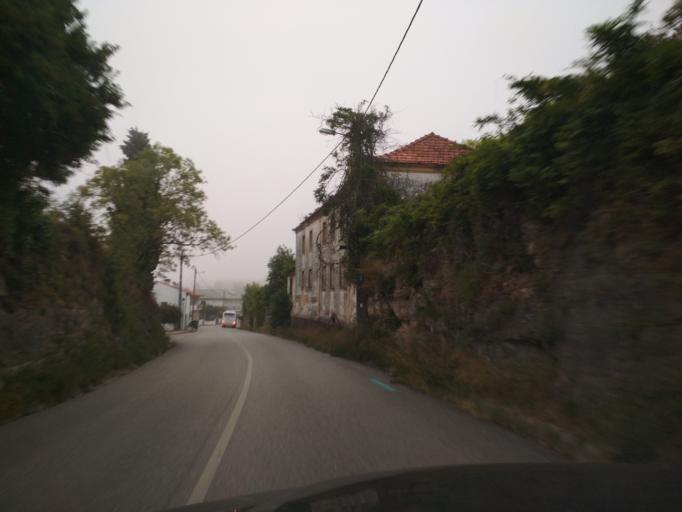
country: PT
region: Coimbra
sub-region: Coimbra
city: Coimbra
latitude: 40.1844
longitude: -8.4429
